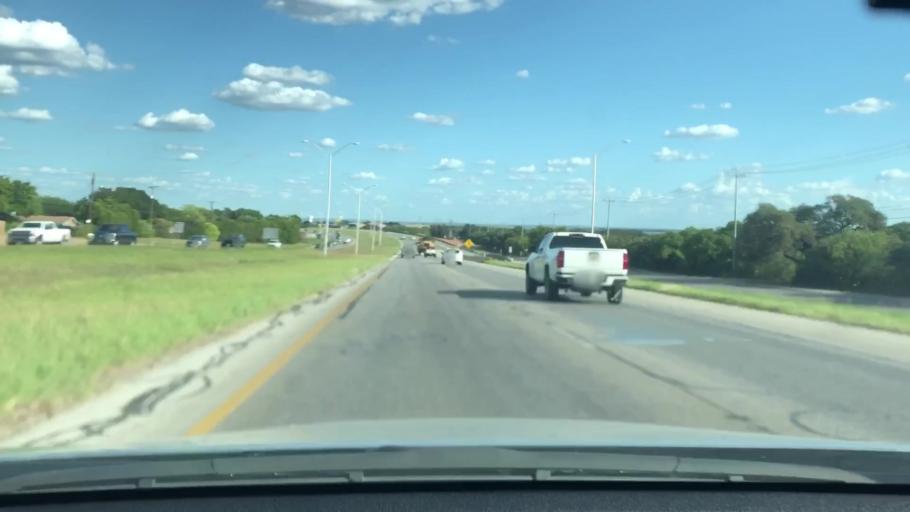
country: US
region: Texas
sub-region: Bexar County
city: Live Oak
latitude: 29.5534
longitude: -98.3219
